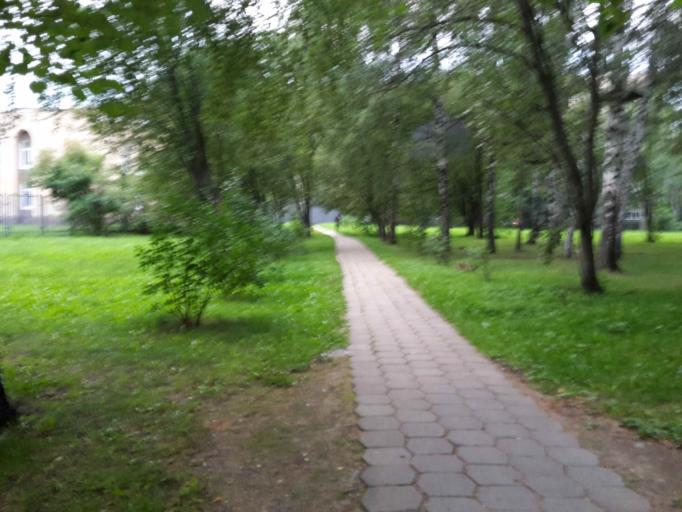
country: RU
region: Moskovskaya
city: Dolgoprudnyy
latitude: 55.9439
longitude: 37.5000
